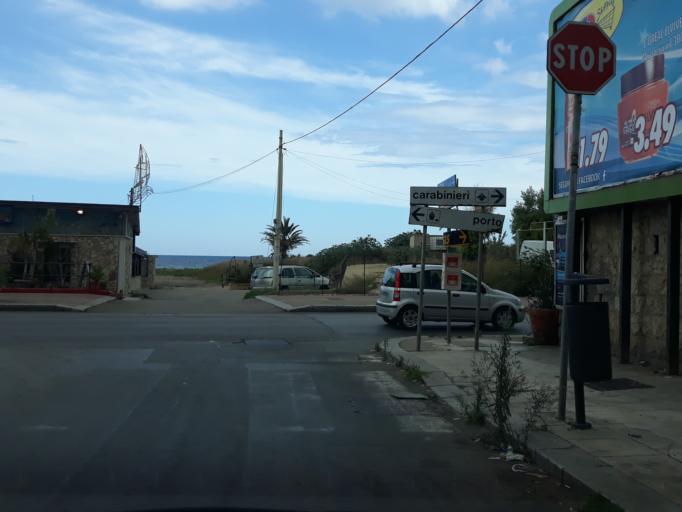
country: IT
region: Sicily
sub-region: Palermo
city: Ciaculli
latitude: 38.1026
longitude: 13.3948
